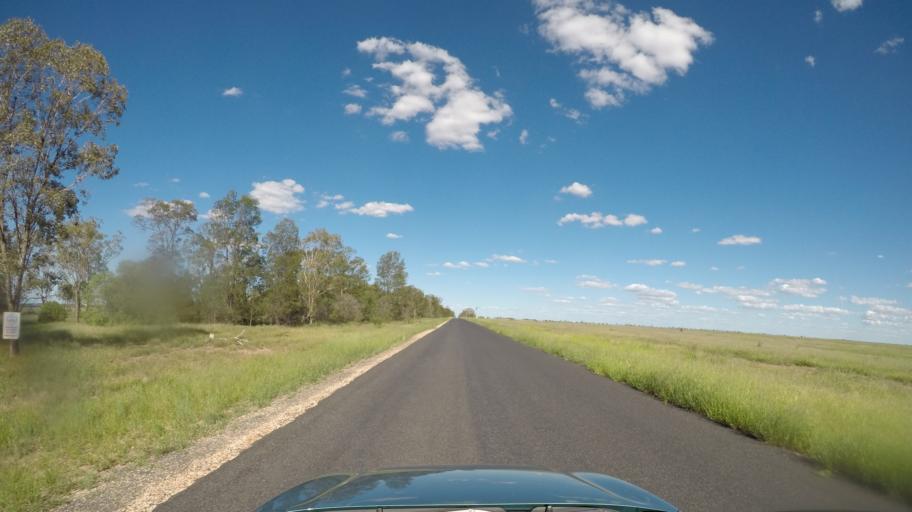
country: AU
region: Queensland
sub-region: Goondiwindi
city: Goondiwindi
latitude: -28.1469
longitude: 150.3013
